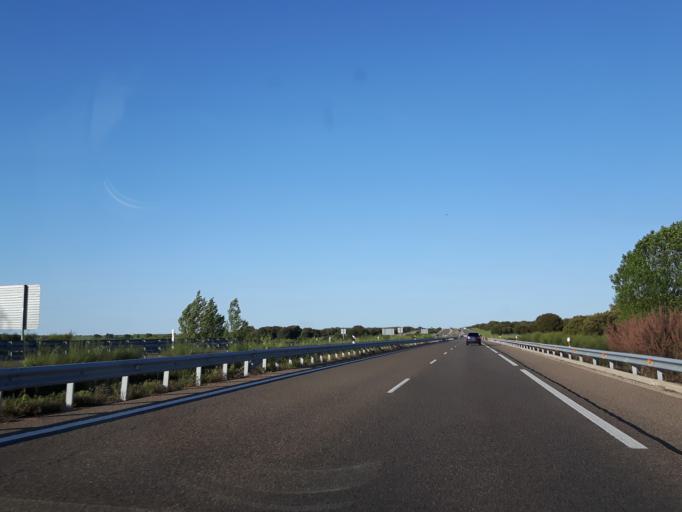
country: ES
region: Castille and Leon
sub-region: Provincia de Salamanca
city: Aldehuela de la Boveda
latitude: 40.8546
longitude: -6.0392
